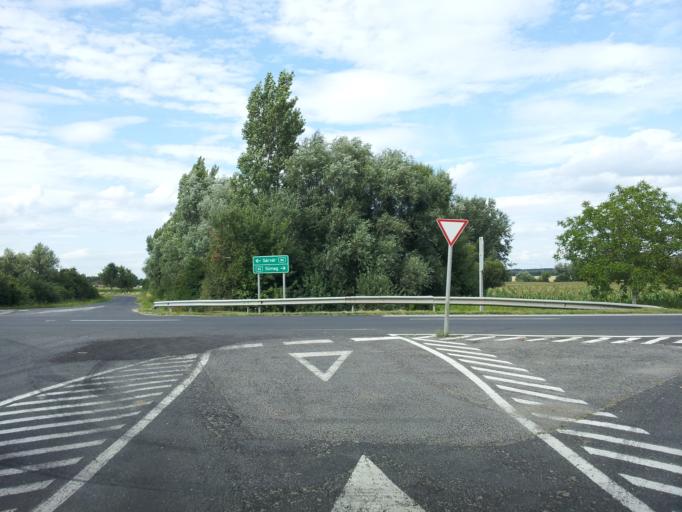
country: HU
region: Vas
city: Janoshaza
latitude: 47.1349
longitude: 17.1059
